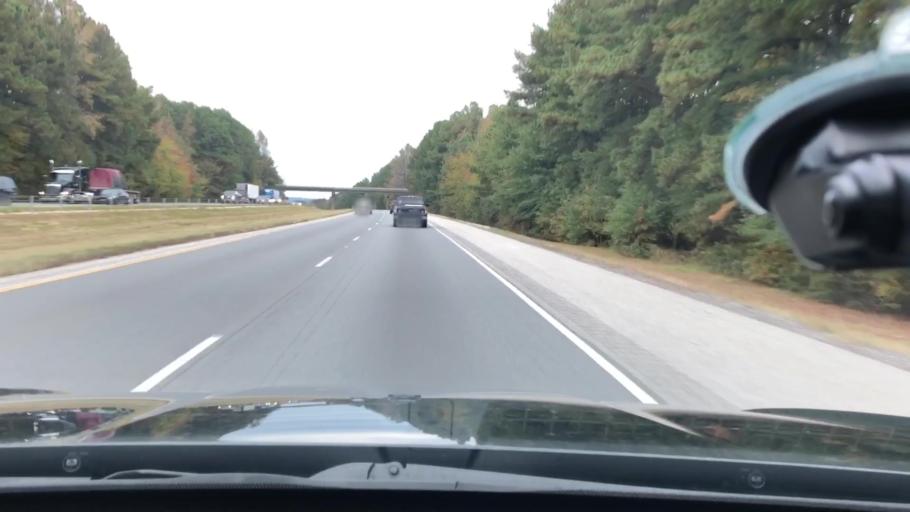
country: US
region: Arkansas
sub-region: Clark County
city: Arkadelphia
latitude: 34.1400
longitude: -93.0813
